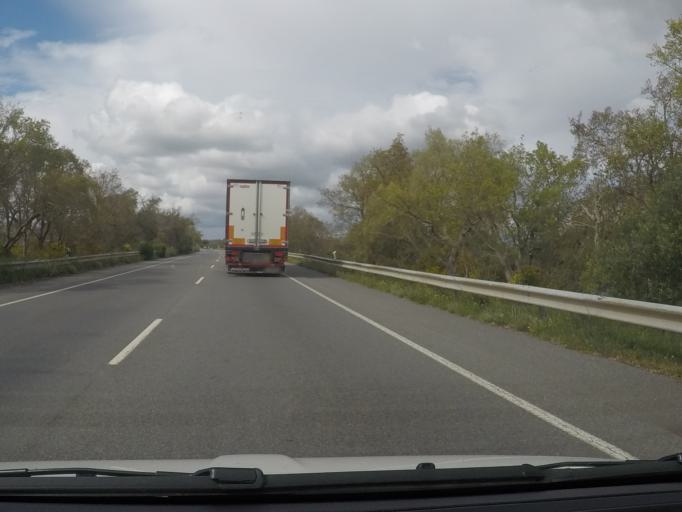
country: PT
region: Setubal
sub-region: Grandola
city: Grandola
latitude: 38.1496
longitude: -8.6497
